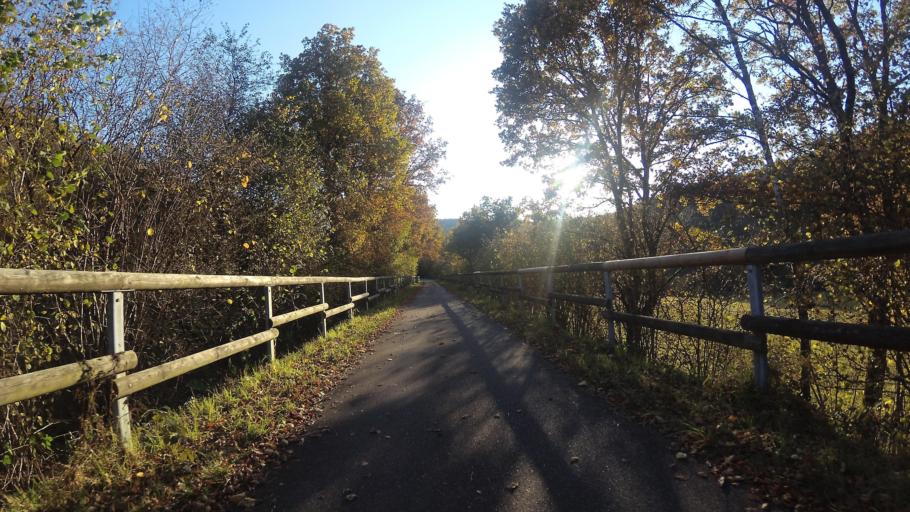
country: DE
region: Rheinland-Pfalz
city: Ollmuth
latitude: 49.6616
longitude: 6.7181
